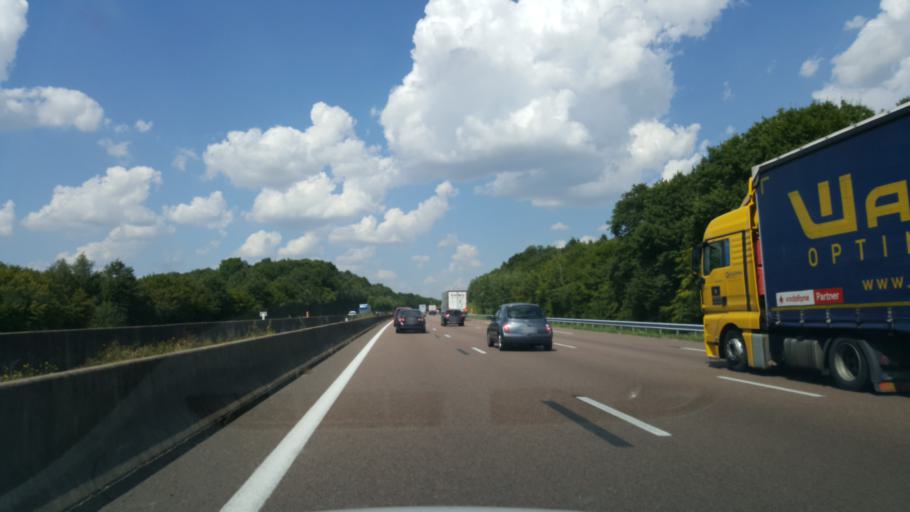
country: FR
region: Bourgogne
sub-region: Departement de Saone-et-Loire
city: Fontaines
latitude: 46.8753
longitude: 4.8188
